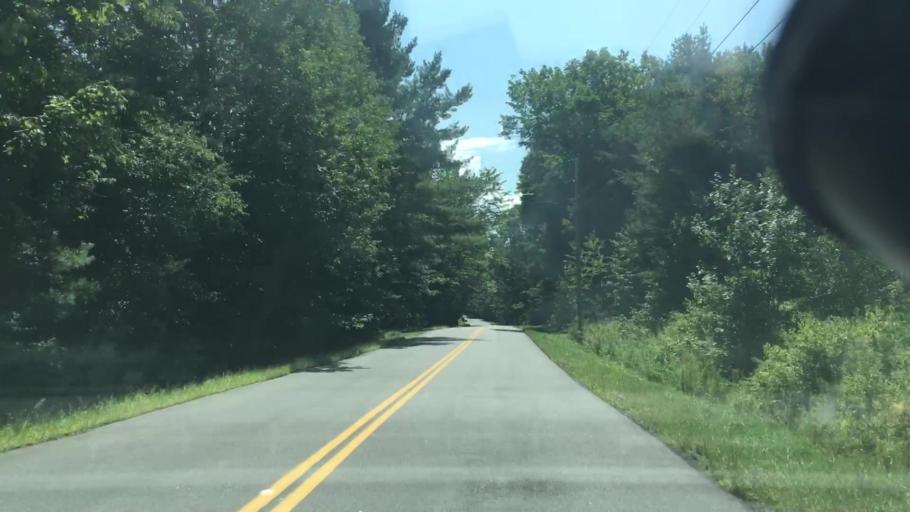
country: US
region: Maine
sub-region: Somerset County
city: Skowhegan
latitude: 44.6940
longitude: -69.6933
